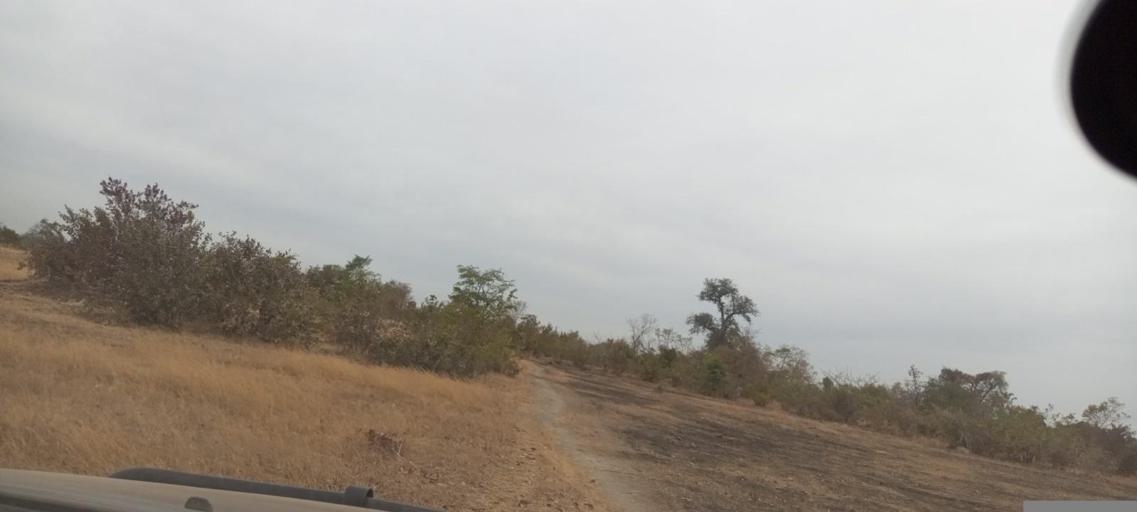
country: ML
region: Koulikoro
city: Kati
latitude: 12.7512
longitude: -8.3606
